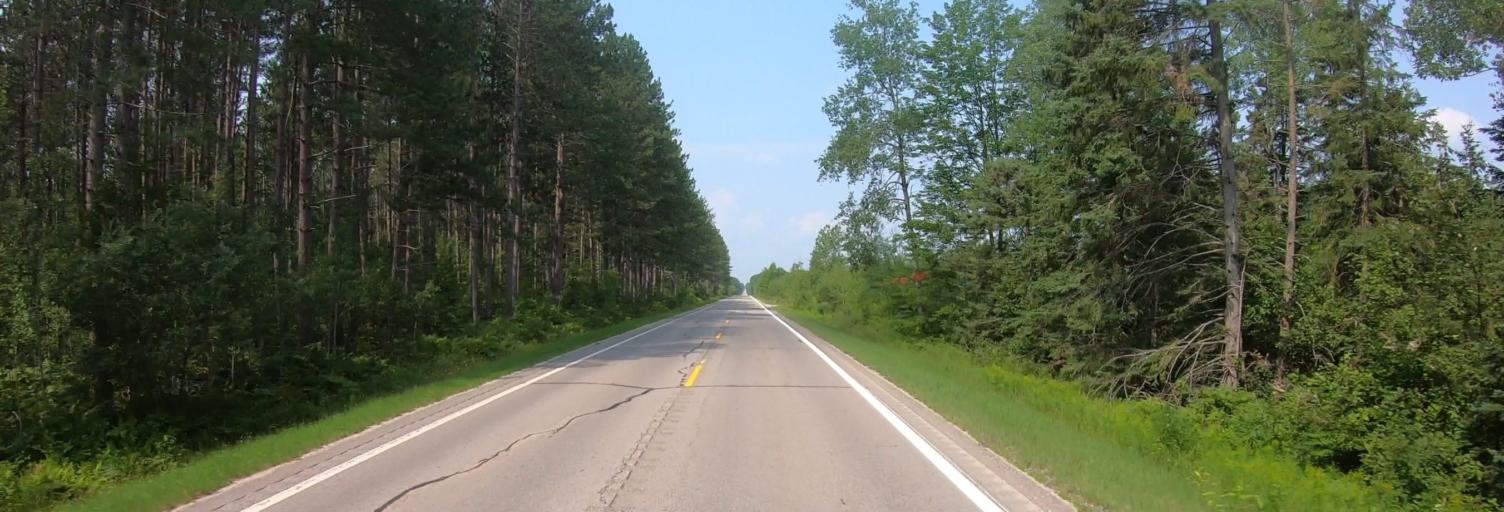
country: US
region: Michigan
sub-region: Luce County
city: Newberry
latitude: 46.5641
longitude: -85.3024
